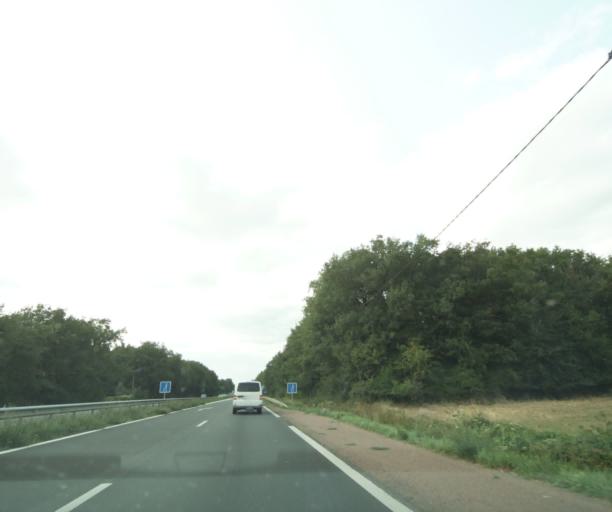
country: FR
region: Centre
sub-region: Departement d'Indre-et-Loire
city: Esvres
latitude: 47.3039
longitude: 0.7930
